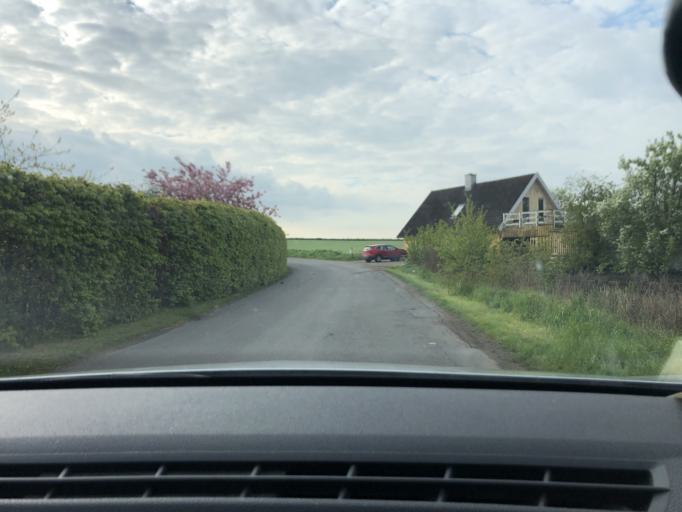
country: DK
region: Zealand
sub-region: Faxe Kommune
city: Ronnede
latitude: 55.2225
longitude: 12.0543
